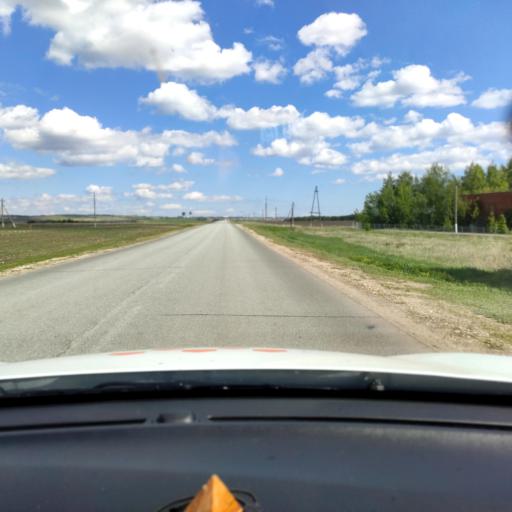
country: RU
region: Tatarstan
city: Kuybyshevskiy Zaton
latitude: 55.1627
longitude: 49.1991
